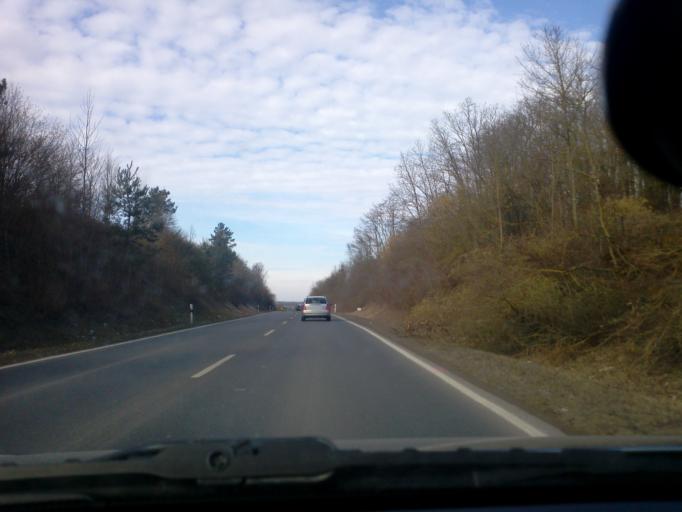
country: DE
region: Baden-Wuerttemberg
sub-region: Regierungsbezirk Stuttgart
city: Gemmingen
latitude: 49.1380
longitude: 8.9972
